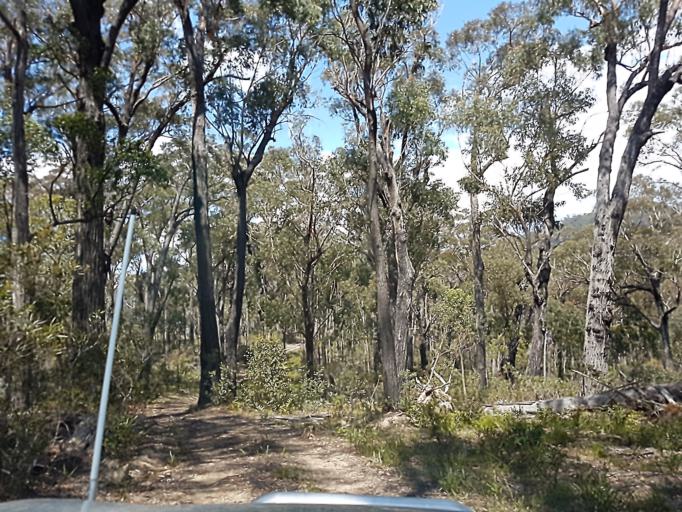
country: AU
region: Victoria
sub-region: East Gippsland
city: Lakes Entrance
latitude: -37.3126
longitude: 148.3440
